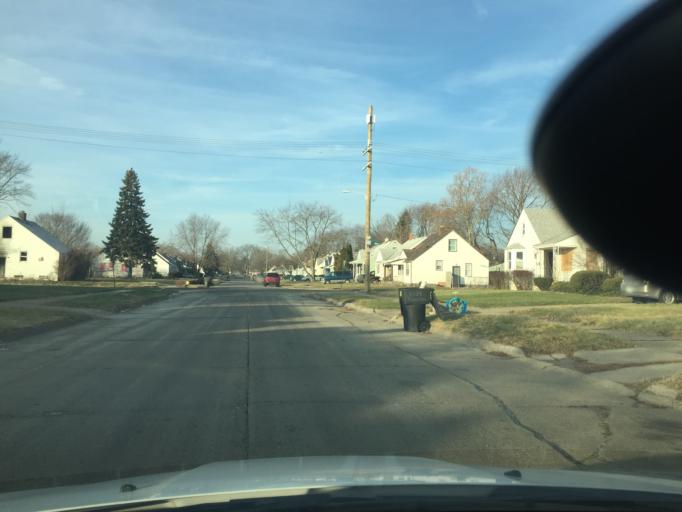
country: US
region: Michigan
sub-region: Macomb County
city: Eastpointe
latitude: 42.4448
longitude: -82.9530
